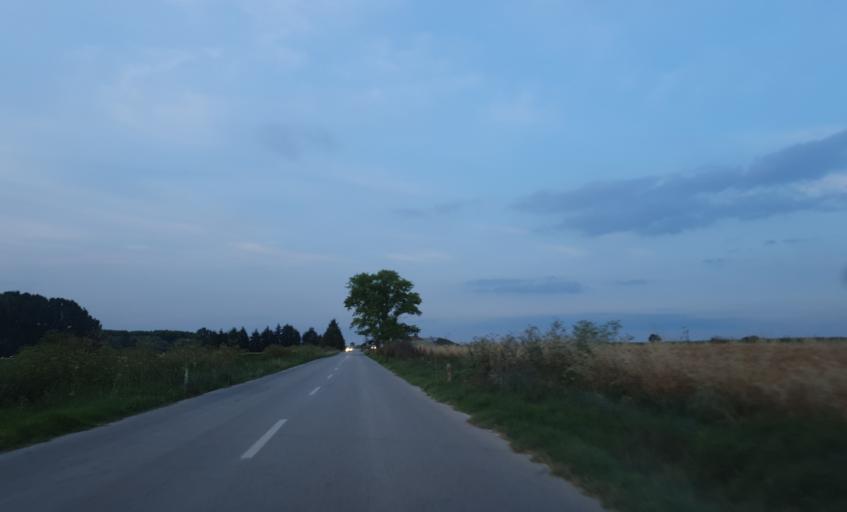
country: TR
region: Tekirdag
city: Beyazkoy
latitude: 41.3923
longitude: 27.6287
